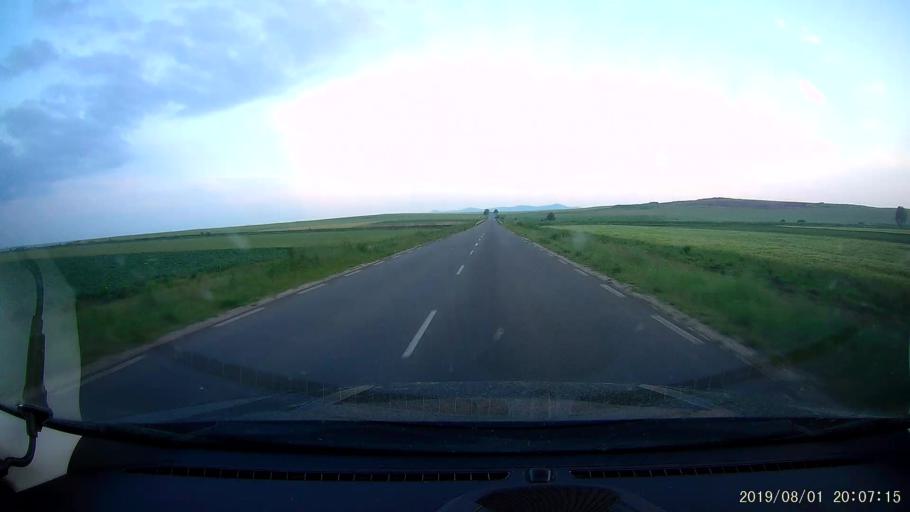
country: BG
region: Yambol
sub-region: Obshtina Yambol
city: Yambol
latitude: 42.5251
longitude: 26.5655
